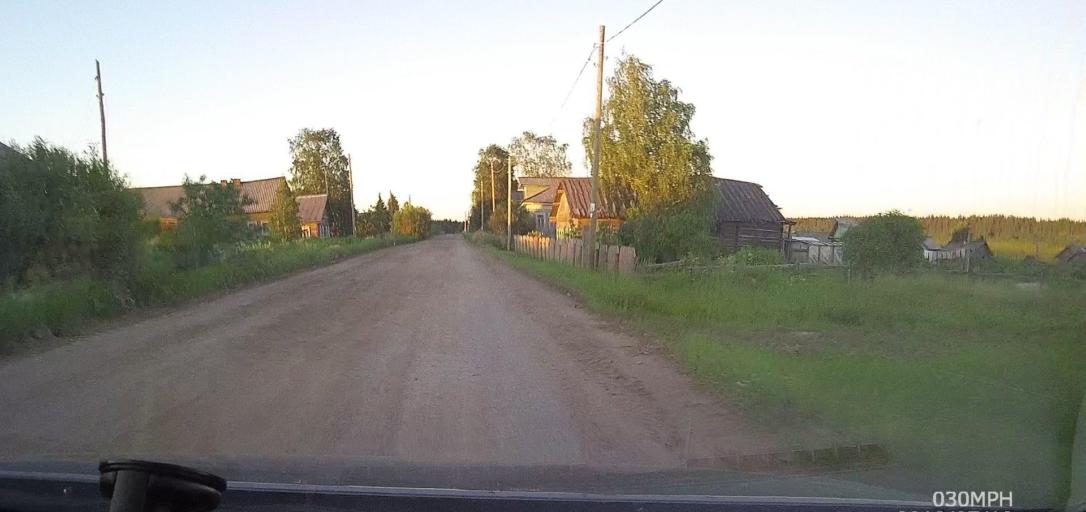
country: RU
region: Arkhangelskaya
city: Lukovetskiy
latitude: 64.2344
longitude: 42.7028
